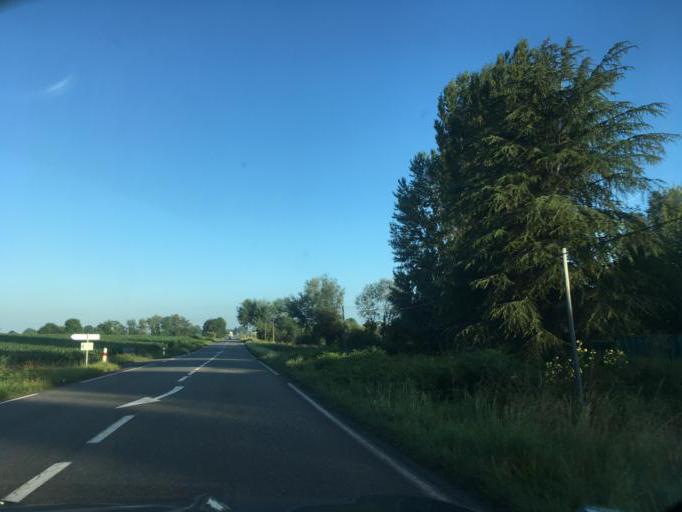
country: FR
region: Aquitaine
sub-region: Departement des Pyrenees-Atlantiques
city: Soumoulou
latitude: 43.2558
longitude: -0.1419
